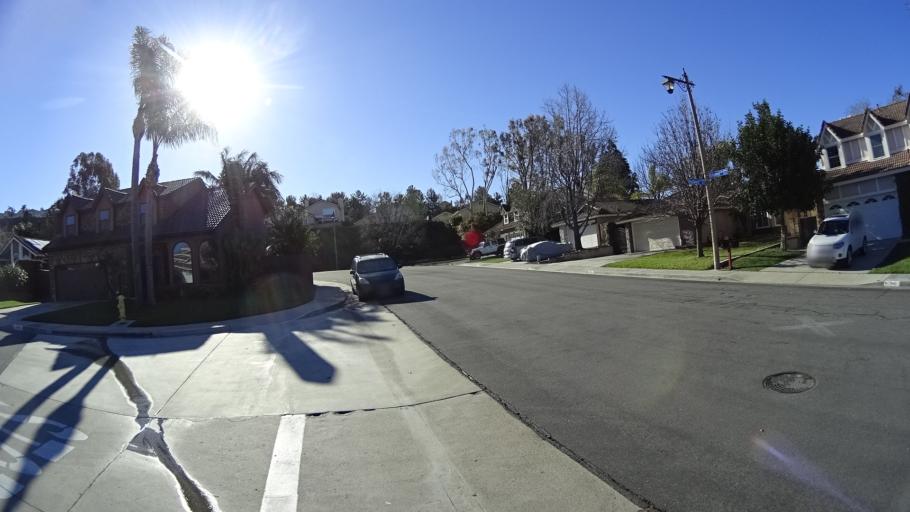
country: US
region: California
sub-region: Orange County
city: Yorba Linda
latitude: 33.8667
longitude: -117.7373
